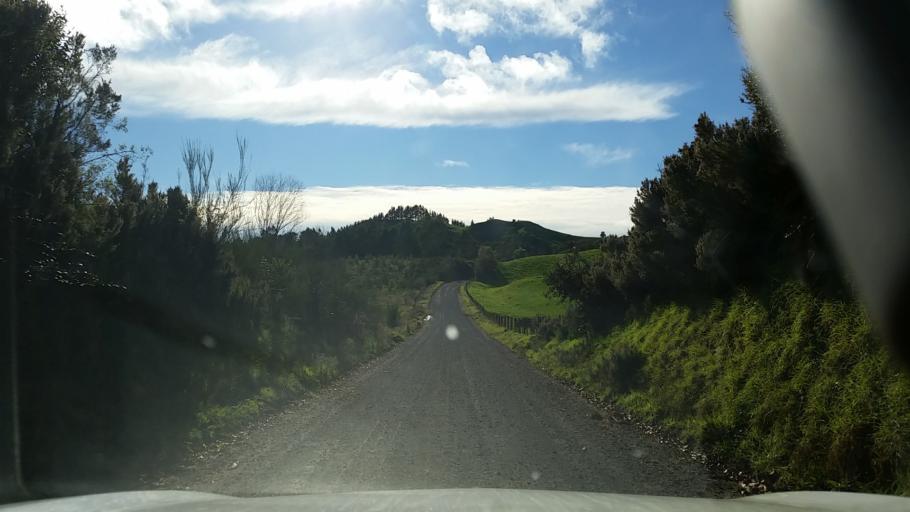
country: NZ
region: Bay of Plenty
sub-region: Rotorua District
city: Rotorua
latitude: -38.3604
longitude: 176.2111
